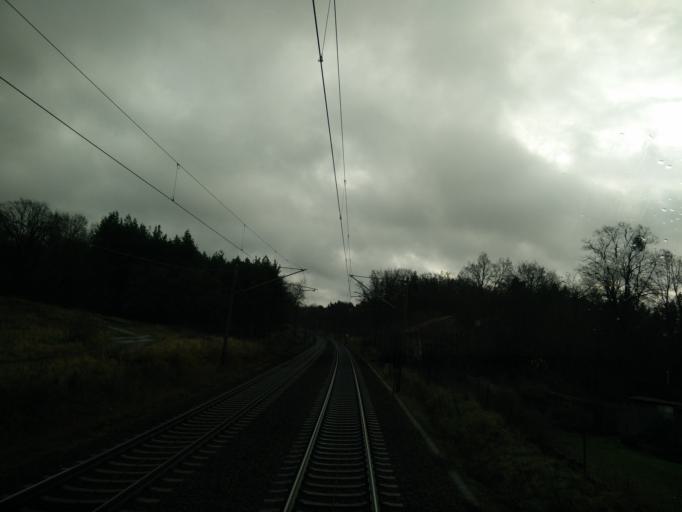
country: DE
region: Mecklenburg-Vorpommern
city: Ludwigslust
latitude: 53.3159
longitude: 11.5108
